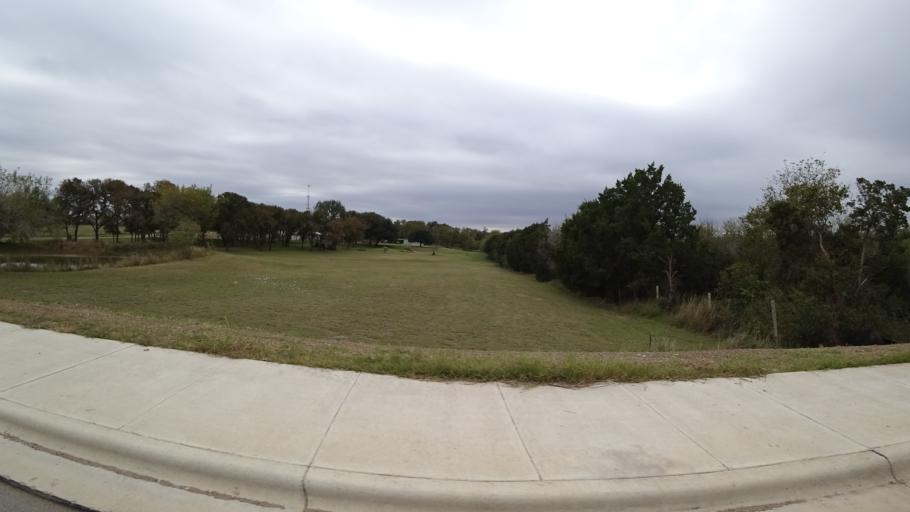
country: US
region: Texas
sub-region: Travis County
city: Manchaca
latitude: 30.1494
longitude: -97.8457
